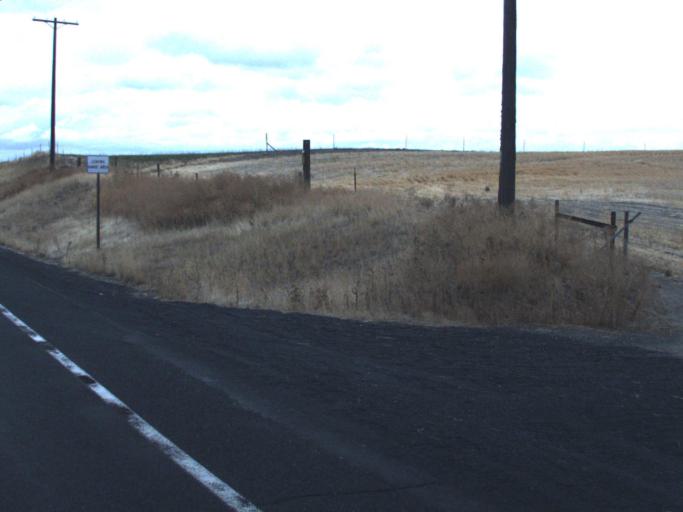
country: US
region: Washington
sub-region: Okanogan County
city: Coulee Dam
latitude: 47.7368
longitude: -118.8502
